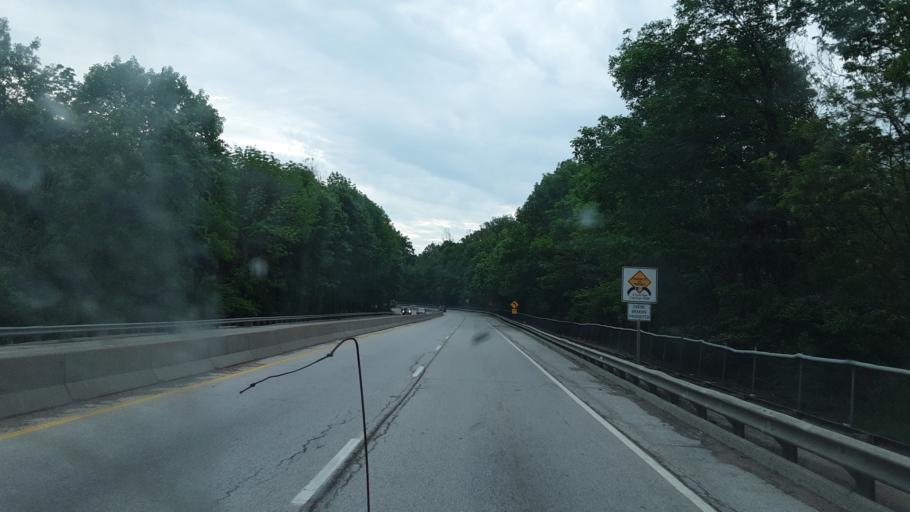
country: US
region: Iowa
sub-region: Lee County
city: Keokuk
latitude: 40.3893
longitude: -91.3702
